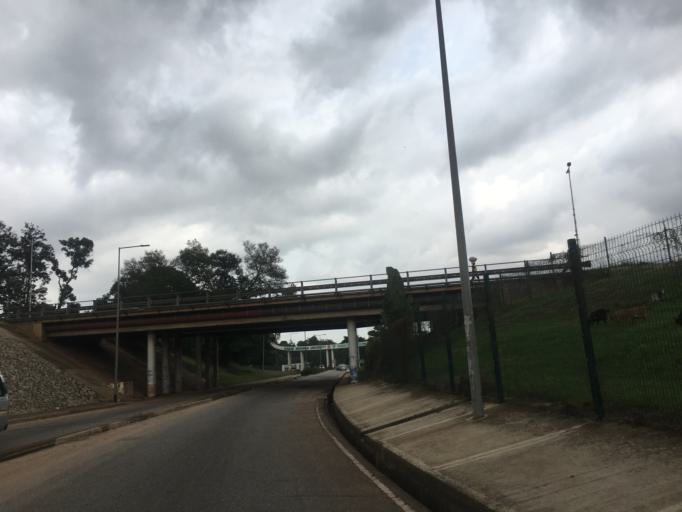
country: GH
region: Ashanti
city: Mamponteng
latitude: 6.6872
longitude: -1.5714
